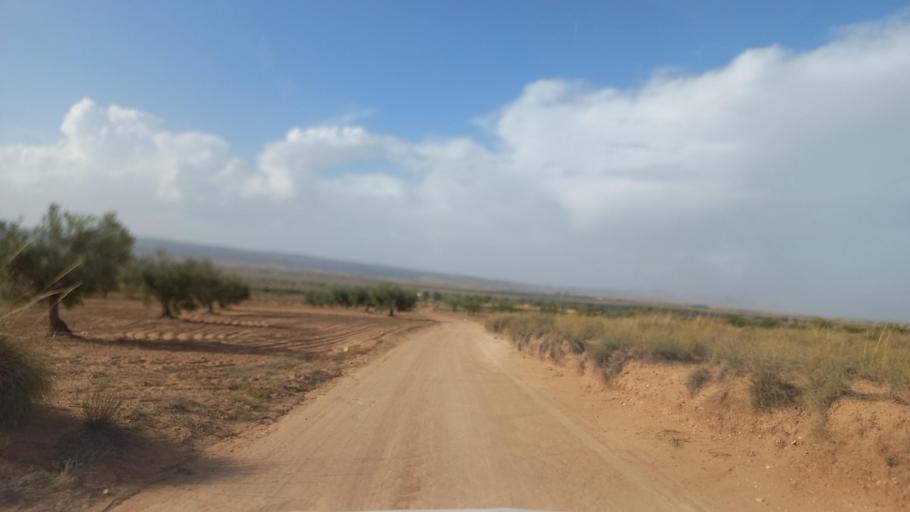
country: TN
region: Al Qasrayn
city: Kasserine
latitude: 35.2174
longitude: 8.9704
